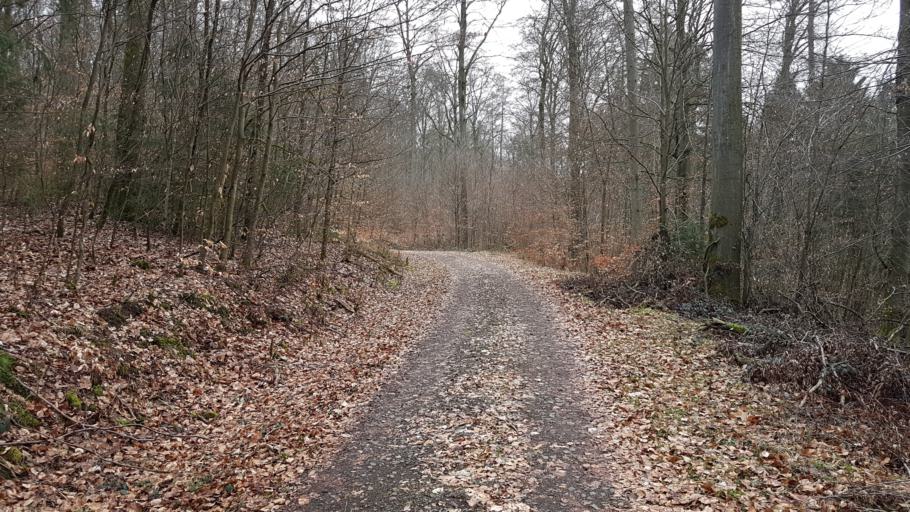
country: DE
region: Saarland
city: Sankt Wendel
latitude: 49.4413
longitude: 7.1788
